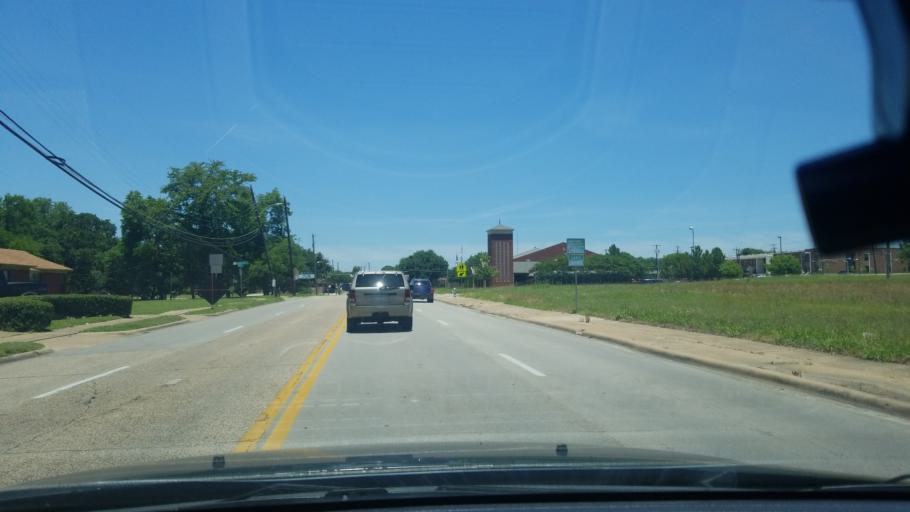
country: US
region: Texas
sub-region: Dallas County
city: Mesquite
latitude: 32.7622
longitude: -96.5987
